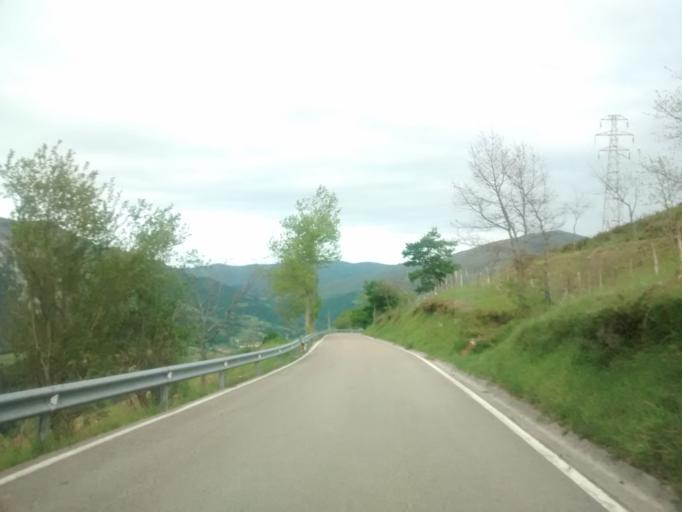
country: ES
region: Cantabria
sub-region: Provincia de Cantabria
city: San Vicente de la Barquera
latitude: 43.2535
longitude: -4.4339
